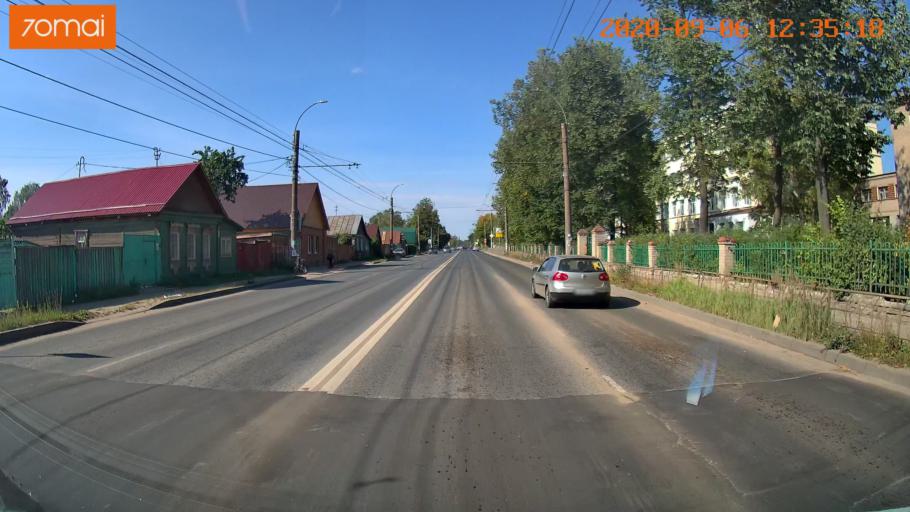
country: RU
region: Ivanovo
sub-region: Gorod Ivanovo
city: Ivanovo
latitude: 57.0194
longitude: 40.9947
